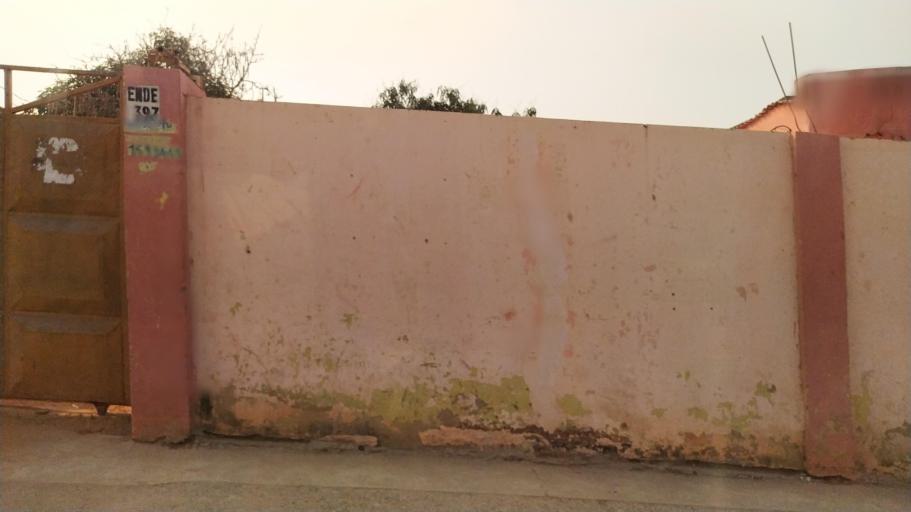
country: AO
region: Luanda
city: Luanda
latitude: -8.8966
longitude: 13.1965
